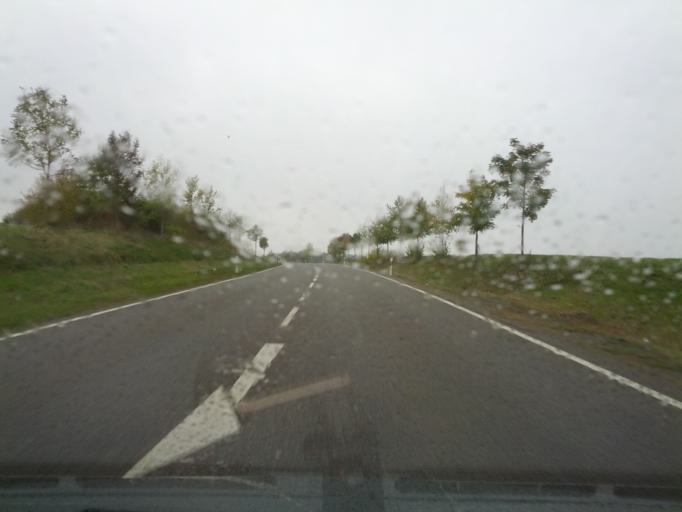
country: DE
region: Saxony
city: Hartenstein
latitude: 50.6729
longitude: 12.6988
